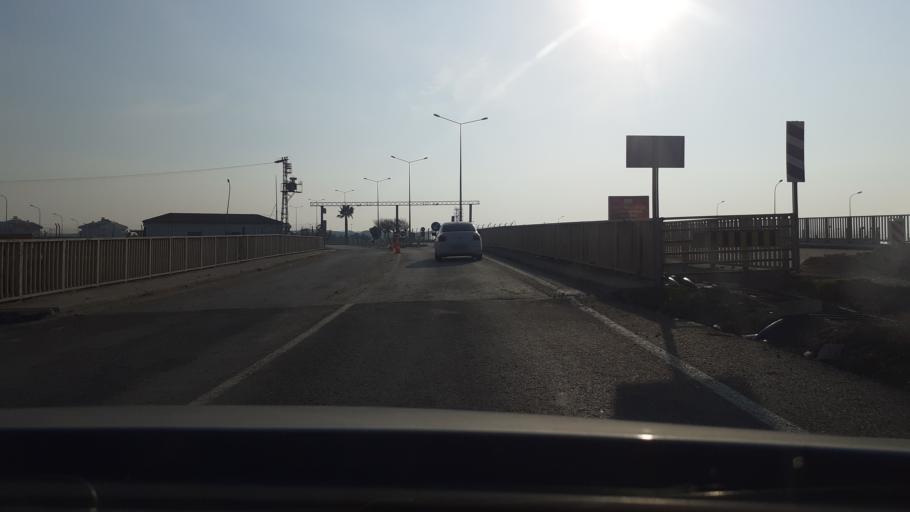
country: TR
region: Hatay
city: Serinyol
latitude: 36.3647
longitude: 36.2724
